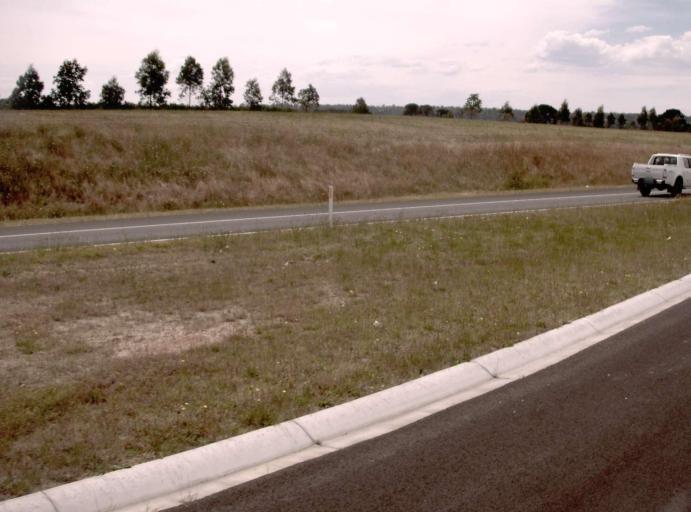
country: AU
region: Victoria
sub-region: Mornington Peninsula
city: Moorooduc
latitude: -38.2297
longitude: 145.1258
